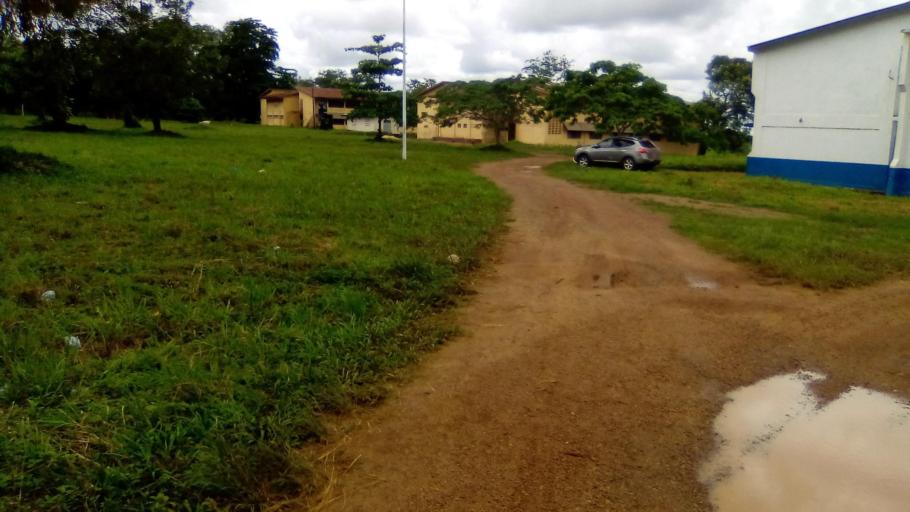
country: SL
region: Southern Province
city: Largo
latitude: 8.1162
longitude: -12.0680
